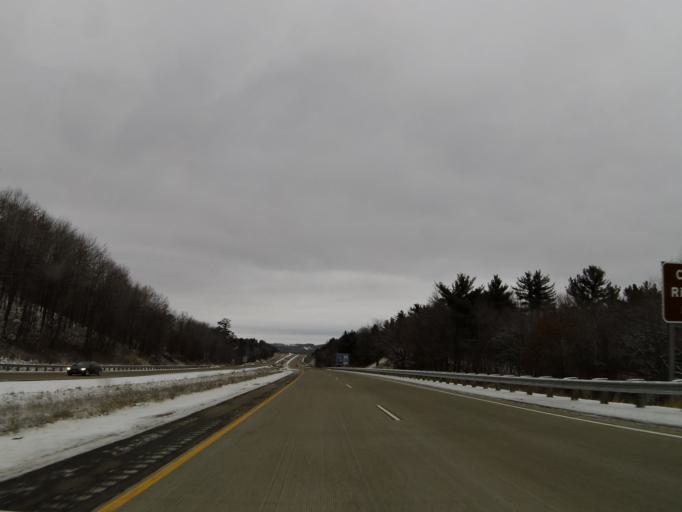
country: US
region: Wisconsin
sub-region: Eau Claire County
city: Eau Claire
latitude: 44.7727
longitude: -91.5170
